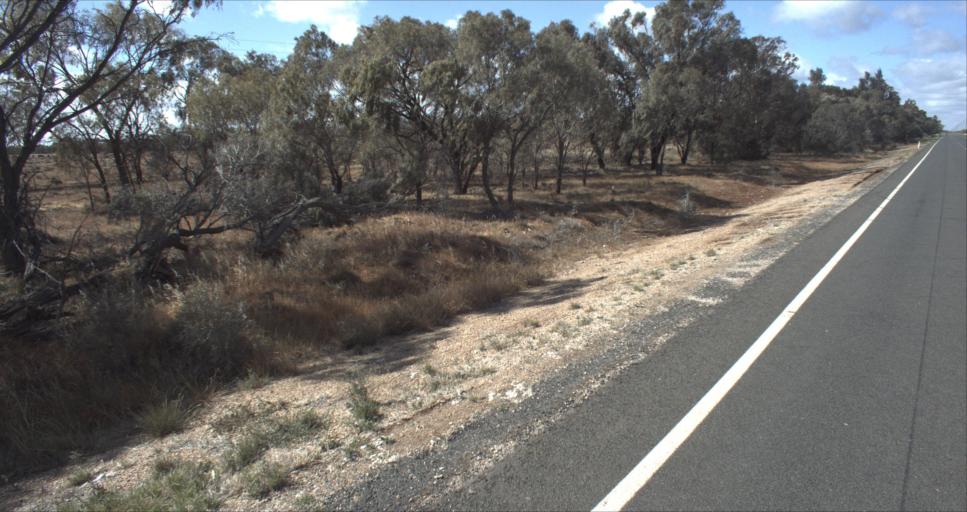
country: AU
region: New South Wales
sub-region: Murrumbidgee Shire
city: Darlington Point
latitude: -34.5268
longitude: 146.1747
